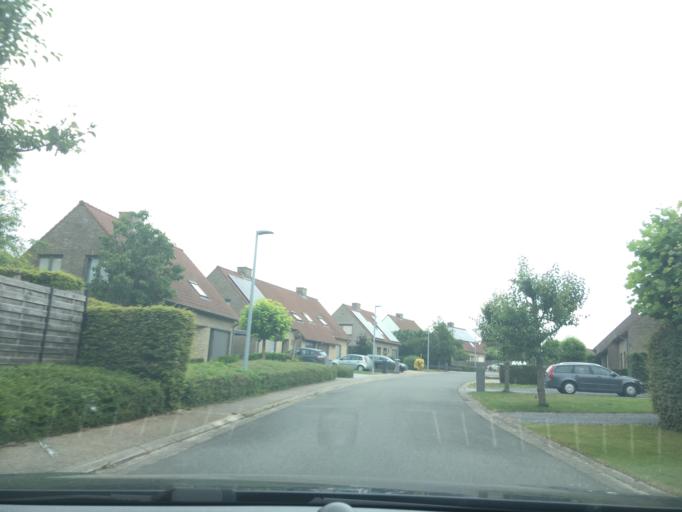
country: BE
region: Flanders
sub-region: Provincie West-Vlaanderen
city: Tielt
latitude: 50.9895
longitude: 3.3240
